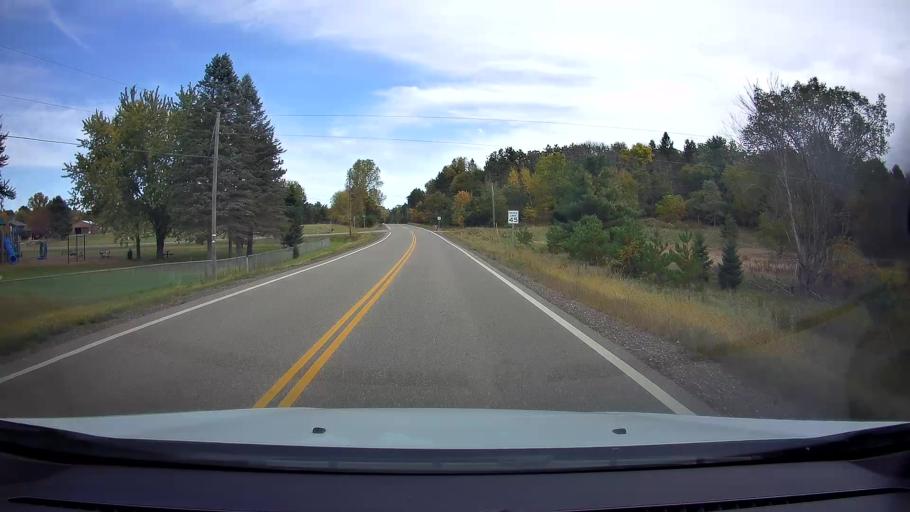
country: US
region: Minnesota
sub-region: Washington County
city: Stillwater
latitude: 45.0786
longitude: -92.8278
